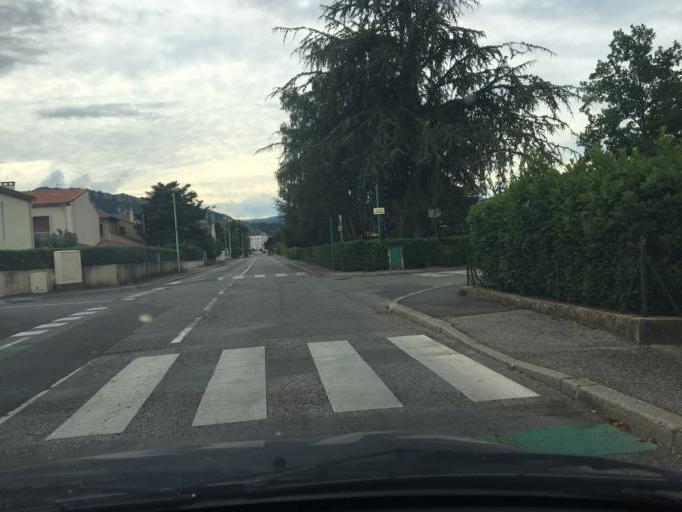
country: FR
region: Rhone-Alpes
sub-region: Departement de l'Ardeche
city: Guilherand-Granges
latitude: 44.9387
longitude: 4.8778
